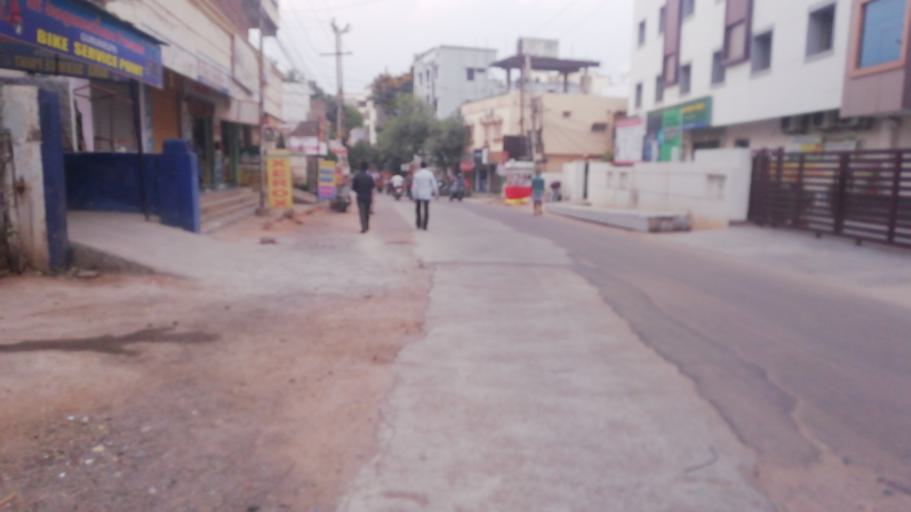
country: IN
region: Telangana
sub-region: Rangareddi
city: Gaddi Annaram
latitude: 17.3633
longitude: 78.5344
